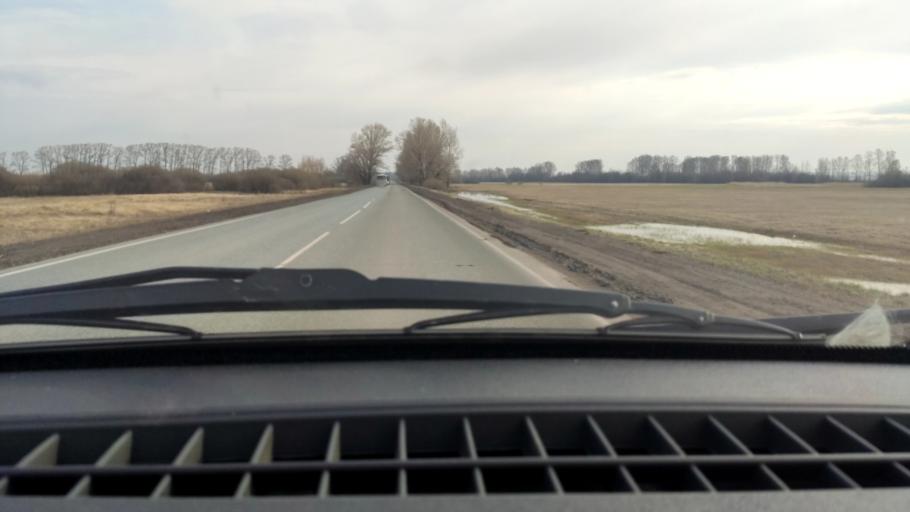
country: RU
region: Bashkortostan
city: Chishmy
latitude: 54.3992
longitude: 55.2111
